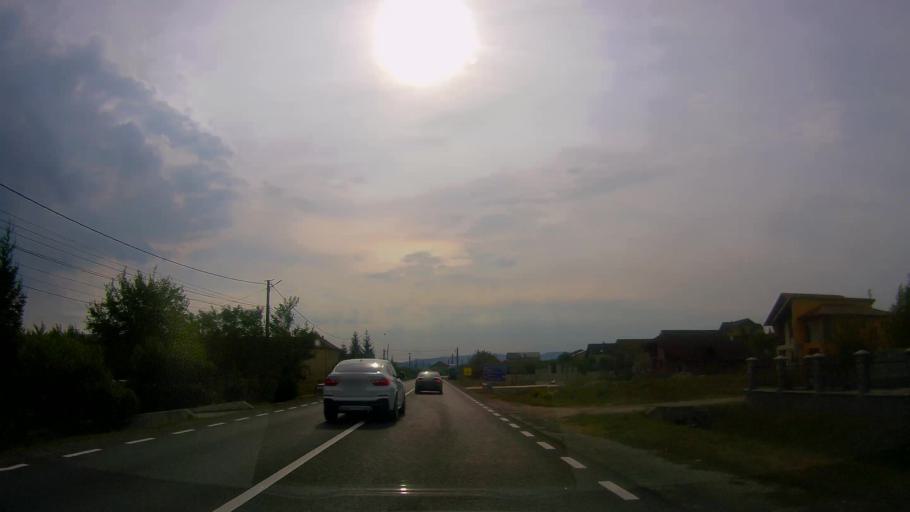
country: RO
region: Salaj
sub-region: Comuna Hereclean
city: Hereclean
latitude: 47.2433
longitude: 22.9904
